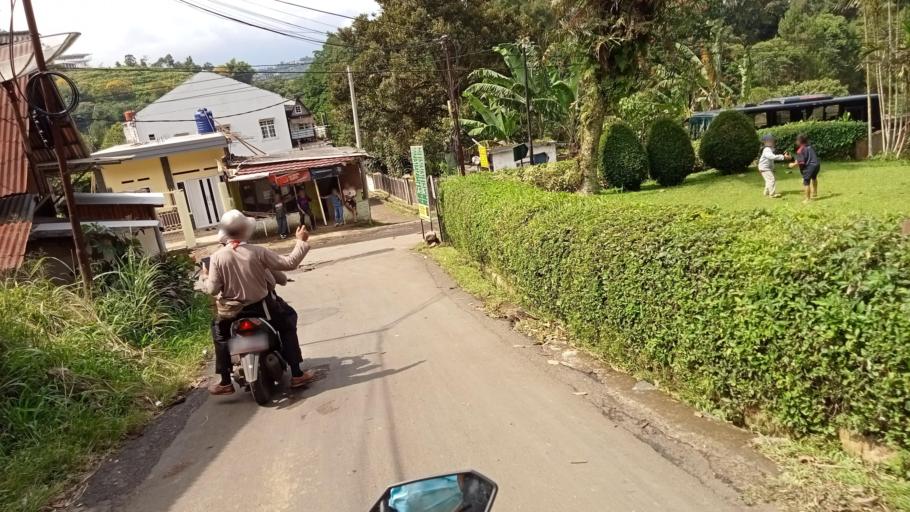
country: ID
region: West Java
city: Caringin
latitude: -6.6444
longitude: 106.9072
